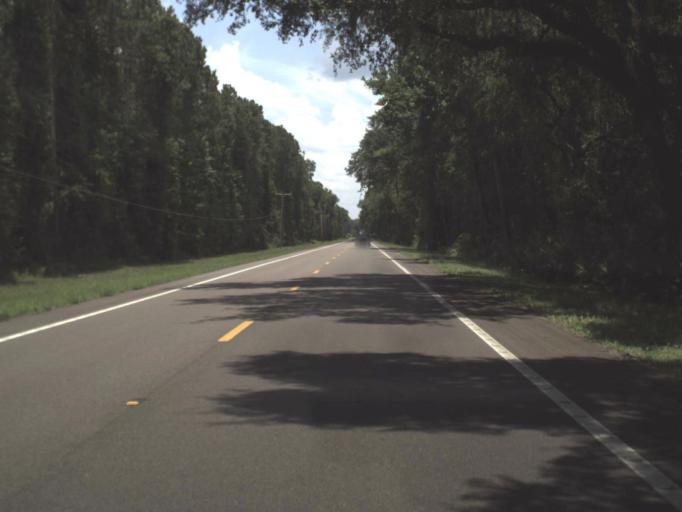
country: US
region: Florida
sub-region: Alachua County
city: Gainesville
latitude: 29.6806
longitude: -82.2329
